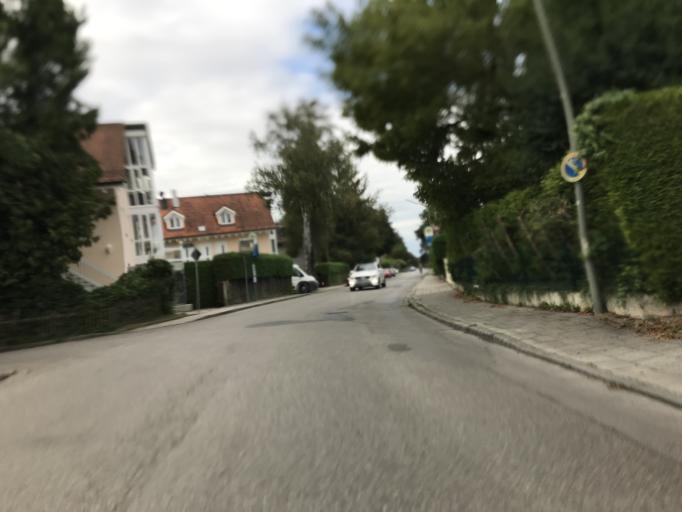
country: DE
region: Bavaria
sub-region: Upper Bavaria
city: Grobenzell
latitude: 48.1866
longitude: 11.3636
